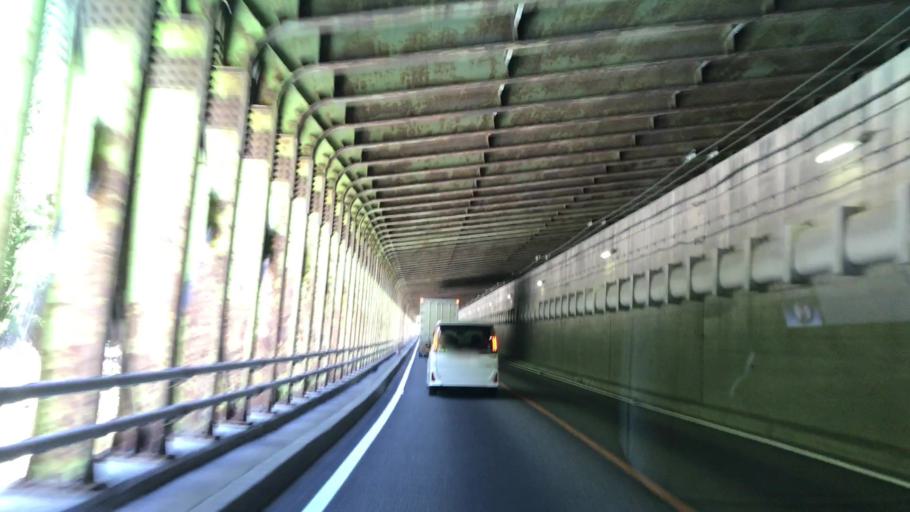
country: JP
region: Hokkaido
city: Shimo-furano
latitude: 42.9428
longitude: 142.5996
